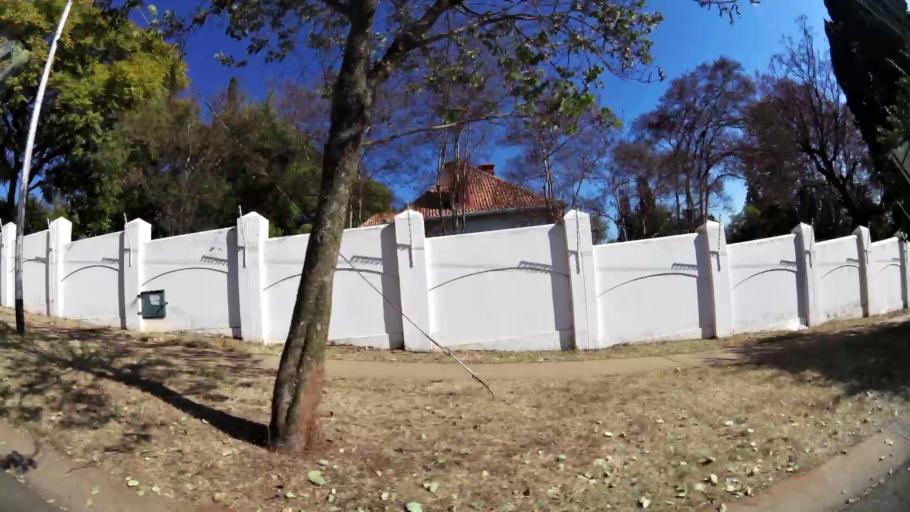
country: ZA
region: Gauteng
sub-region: City of Tshwane Metropolitan Municipality
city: Pretoria
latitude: -25.7628
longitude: 28.2045
